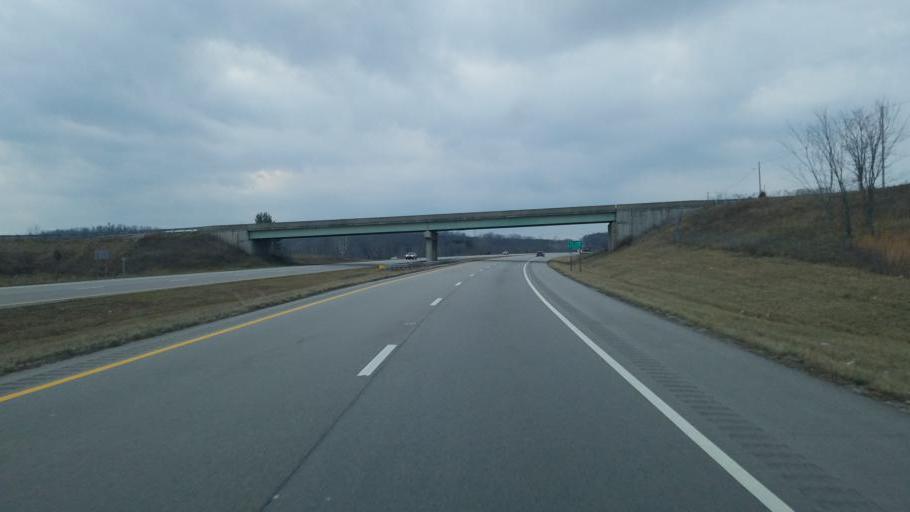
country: US
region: Ohio
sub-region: Jackson County
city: Oak Hill
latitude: 38.8846
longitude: -82.4198
